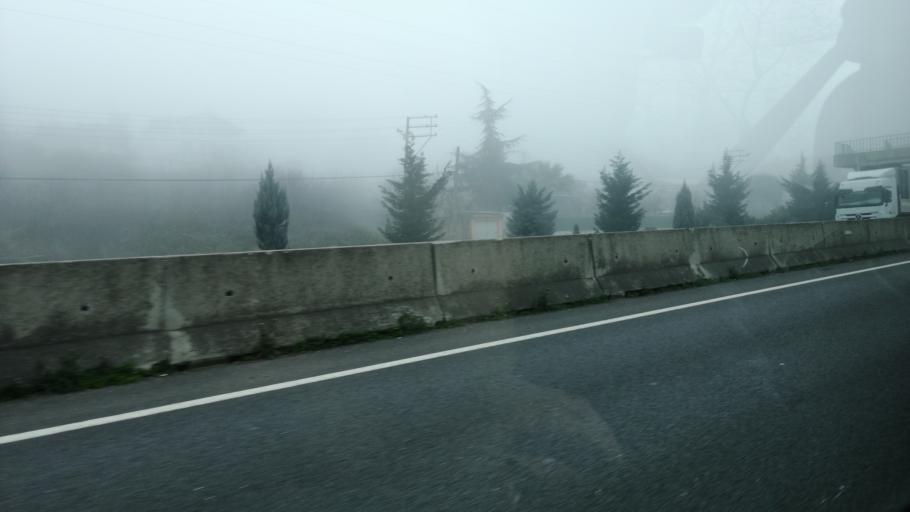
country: TR
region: Yalova
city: Ciftlikkoy
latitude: 40.6730
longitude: 29.3442
